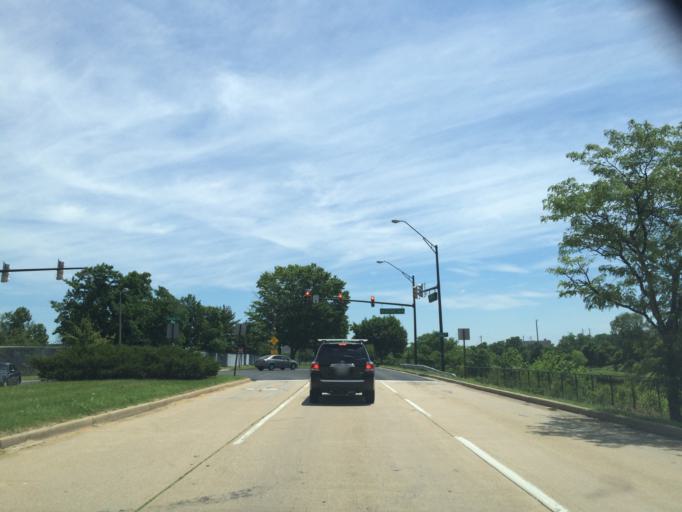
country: US
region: Virginia
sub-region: Fairfax County
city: Huntington
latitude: 38.8034
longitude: -77.0918
